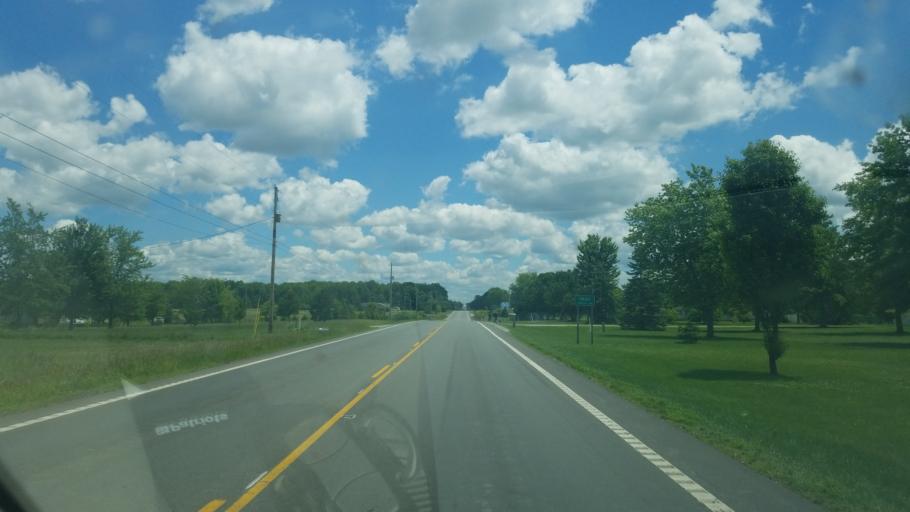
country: US
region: Ohio
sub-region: Huron County
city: New London
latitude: 41.0295
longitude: -82.3362
